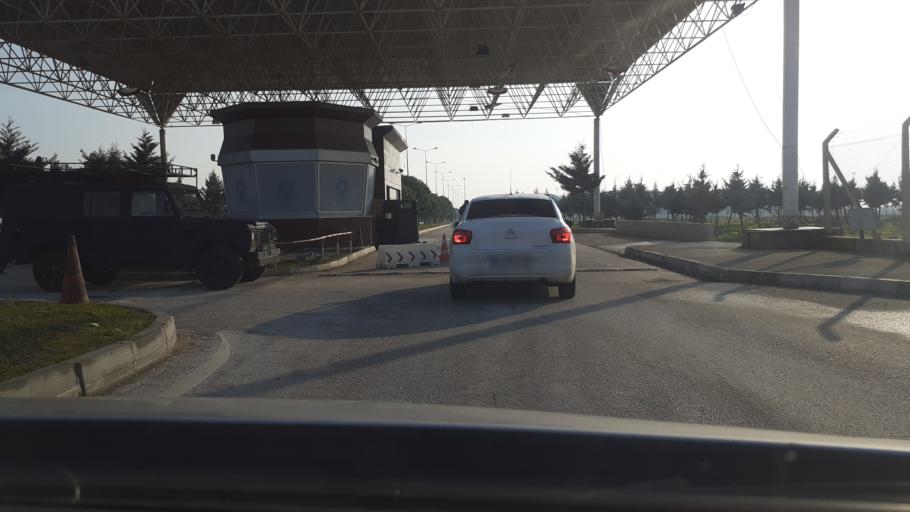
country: TR
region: Hatay
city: Serinyol
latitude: 36.3644
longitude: 36.2759
